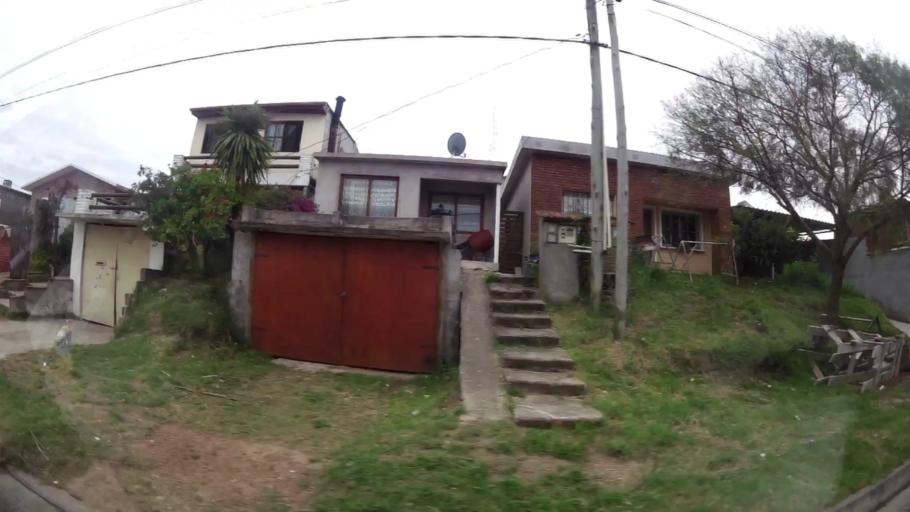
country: UY
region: Maldonado
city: Maldonado
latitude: -34.8873
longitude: -54.9391
